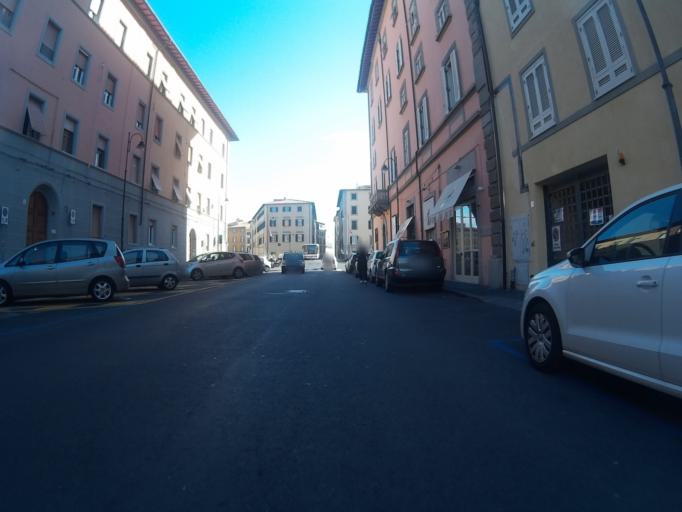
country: IT
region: Tuscany
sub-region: Provincia di Livorno
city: Livorno
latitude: 43.5538
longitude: 10.3057
